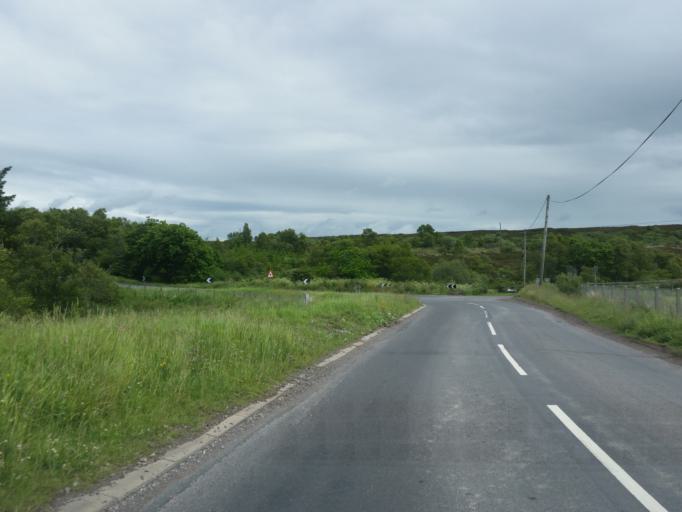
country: IE
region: Ulster
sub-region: County Monaghan
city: Monaghan
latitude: 54.5058
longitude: -7.0464
